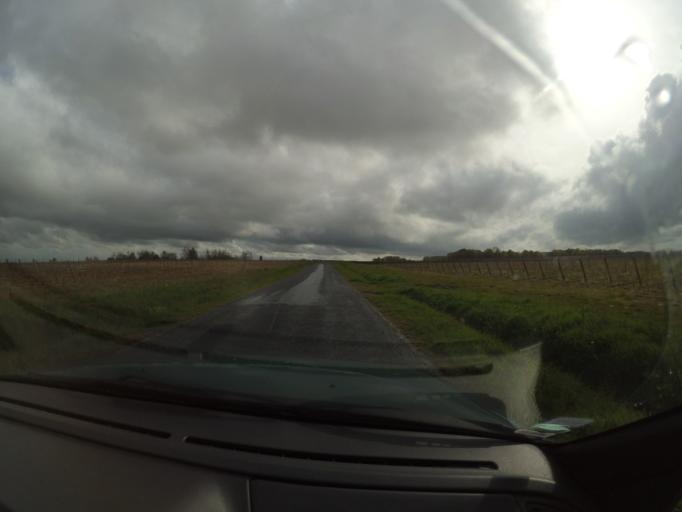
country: FR
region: Pays de la Loire
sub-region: Departement de la Loire-Atlantique
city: Monnieres
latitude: 47.1255
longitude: -1.3545
